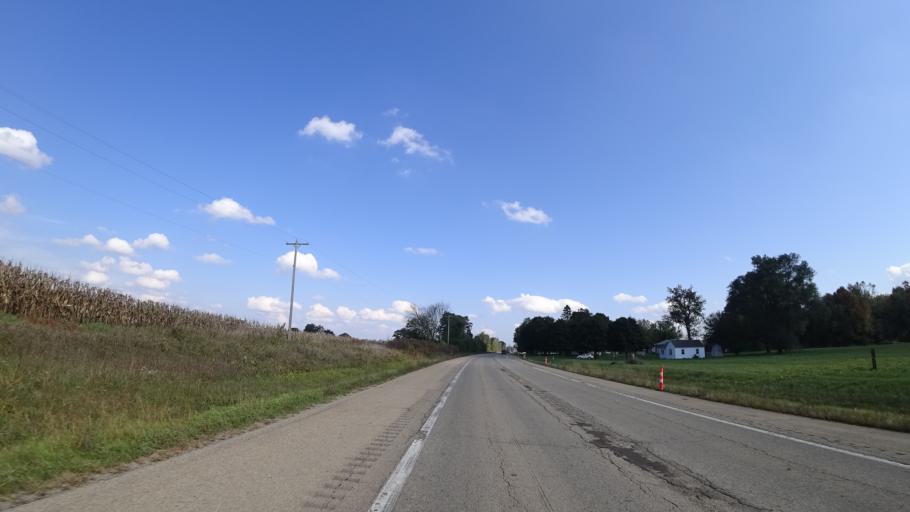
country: US
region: Michigan
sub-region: Calhoun County
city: Homer
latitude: 42.1451
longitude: -84.8443
